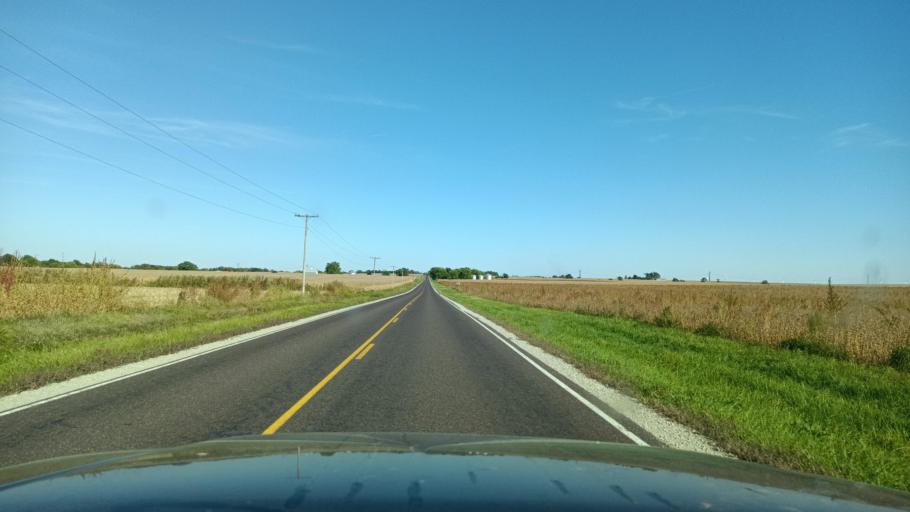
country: US
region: Illinois
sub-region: Logan County
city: Atlanta
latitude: 40.2386
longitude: -89.1070
